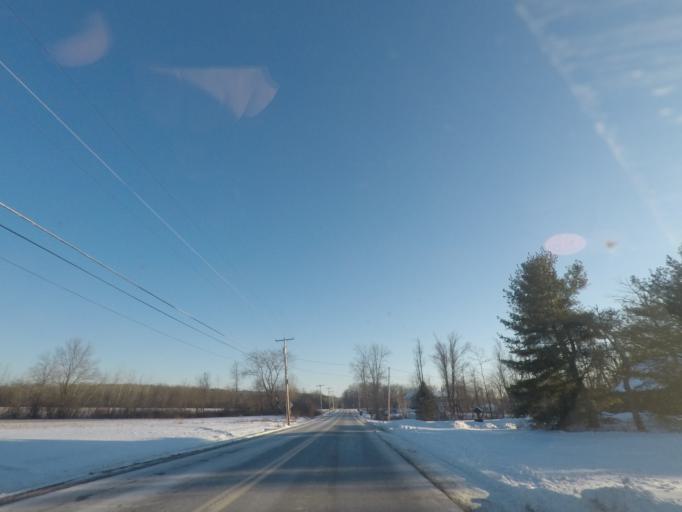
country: US
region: New York
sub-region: Saratoga County
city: Waterford
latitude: 42.8463
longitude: -73.6700
